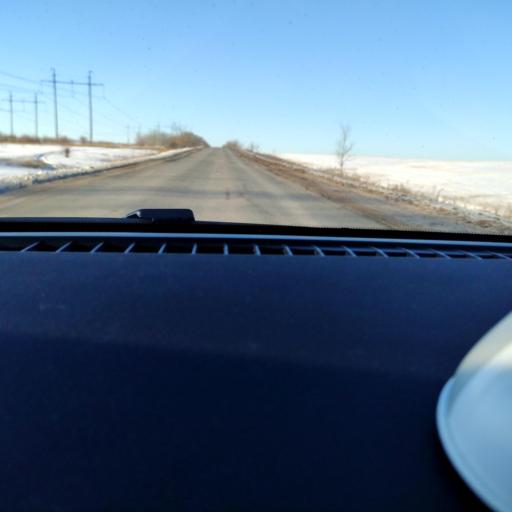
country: RU
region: Samara
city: Spiridonovka
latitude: 53.1446
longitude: 50.5447
